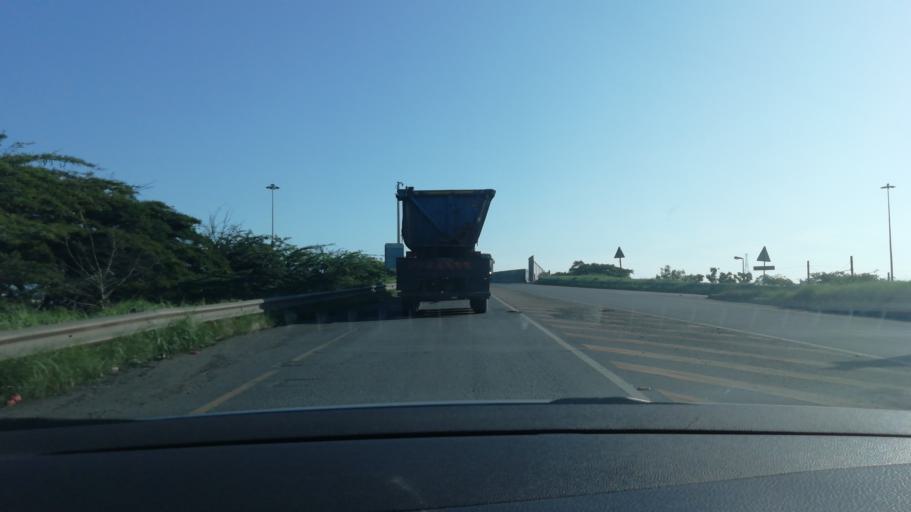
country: ZA
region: KwaZulu-Natal
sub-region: uThungulu District Municipality
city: Richards Bay
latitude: -28.7811
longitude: 32.0285
